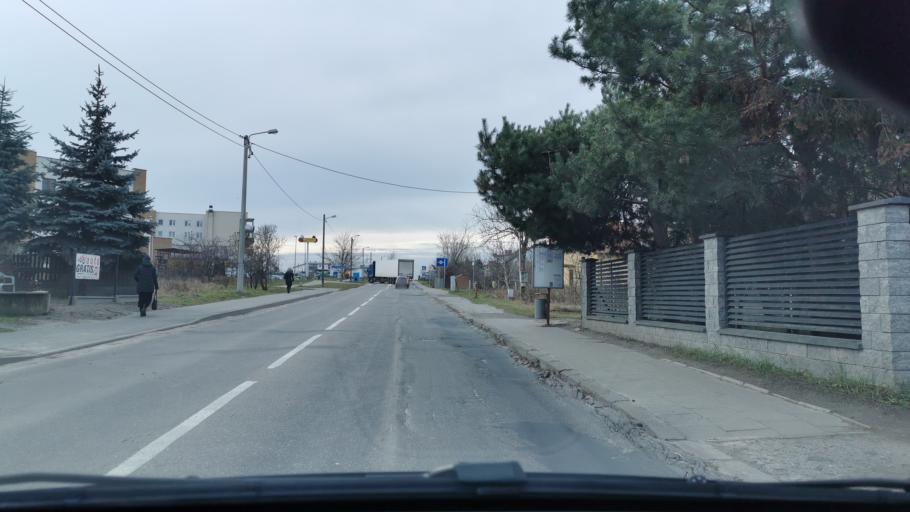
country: PL
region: Lublin Voivodeship
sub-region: Powiat lubelski
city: Lublin
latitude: 51.2000
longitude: 22.5421
